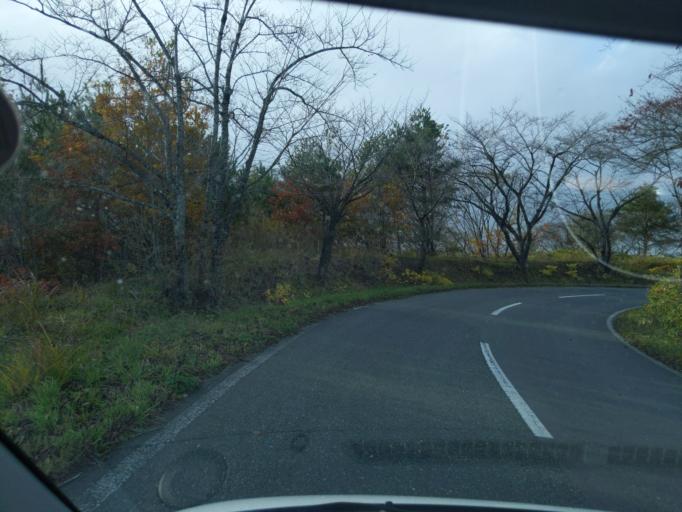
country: JP
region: Iwate
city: Mizusawa
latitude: 39.0392
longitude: 141.0797
